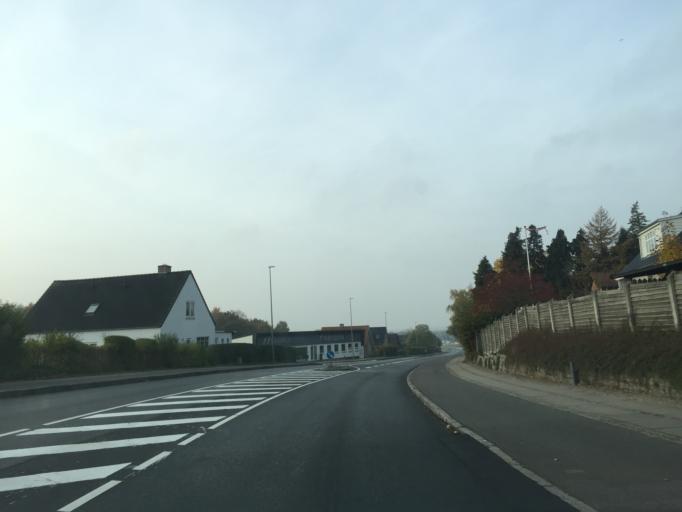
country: DK
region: Central Jutland
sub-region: Silkeborg Kommune
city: Silkeborg
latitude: 56.1907
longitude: 9.5813
